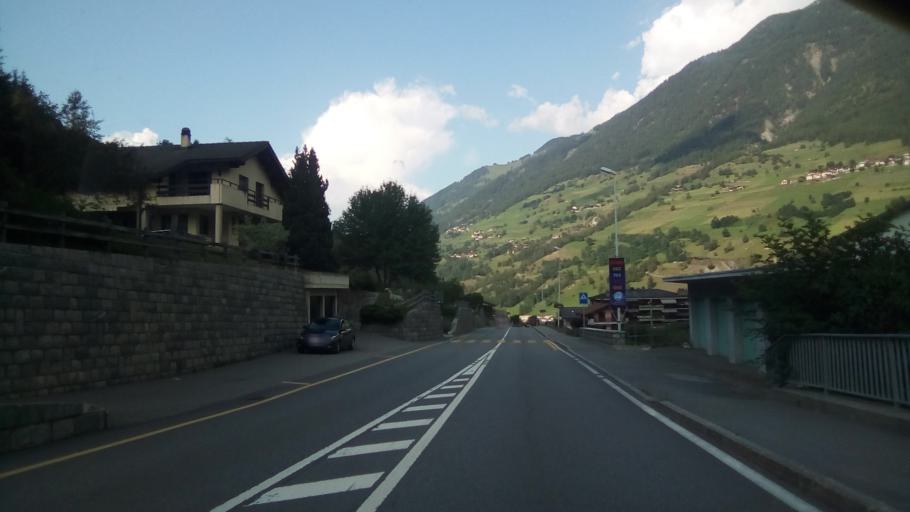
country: CH
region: Valais
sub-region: Entremont District
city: Orsieres
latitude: 46.0236
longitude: 7.1387
